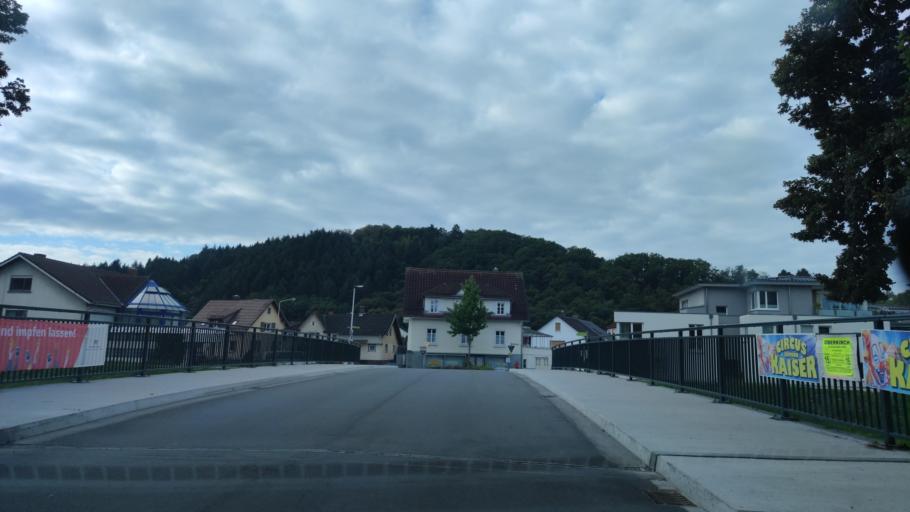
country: DE
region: Baden-Wuerttemberg
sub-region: Freiburg Region
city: Oberkirch
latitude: 48.5272
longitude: 8.0776
